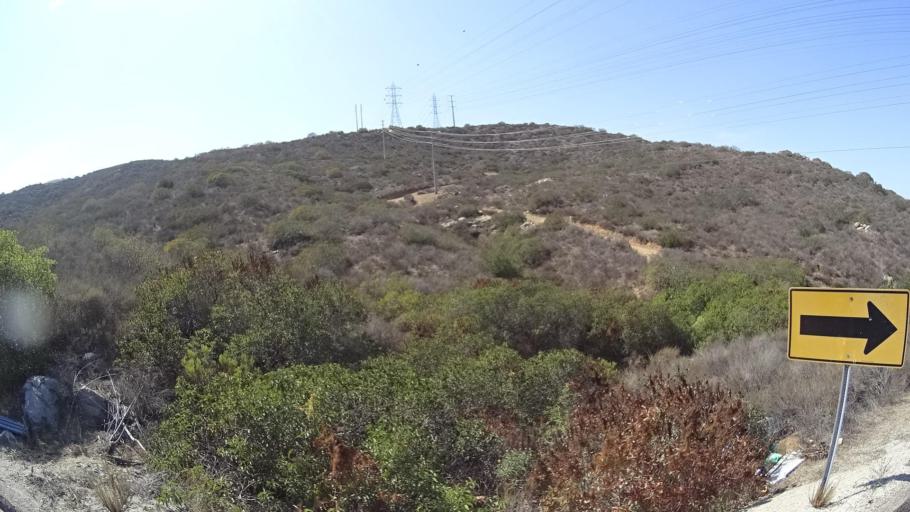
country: US
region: California
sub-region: San Diego County
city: Rancho San Diego
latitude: 32.7215
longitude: -116.9303
